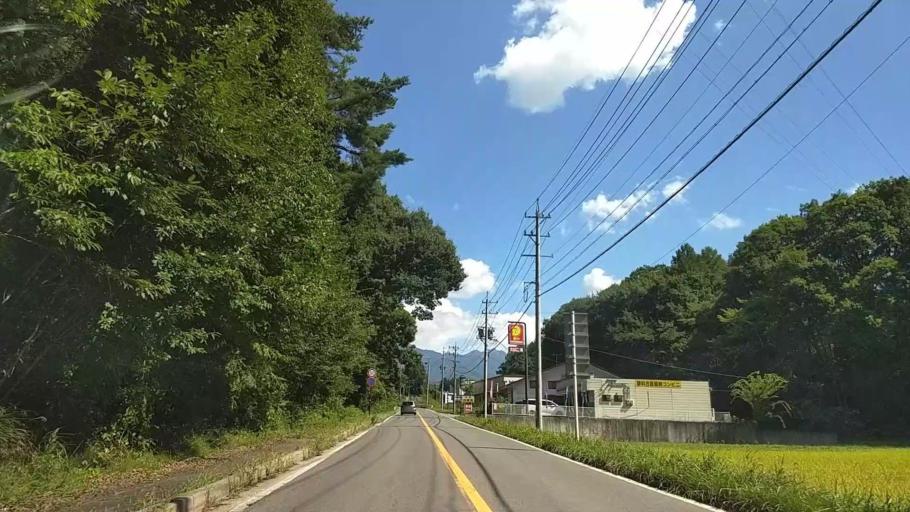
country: JP
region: Nagano
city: Chino
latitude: 36.0320
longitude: 138.2059
